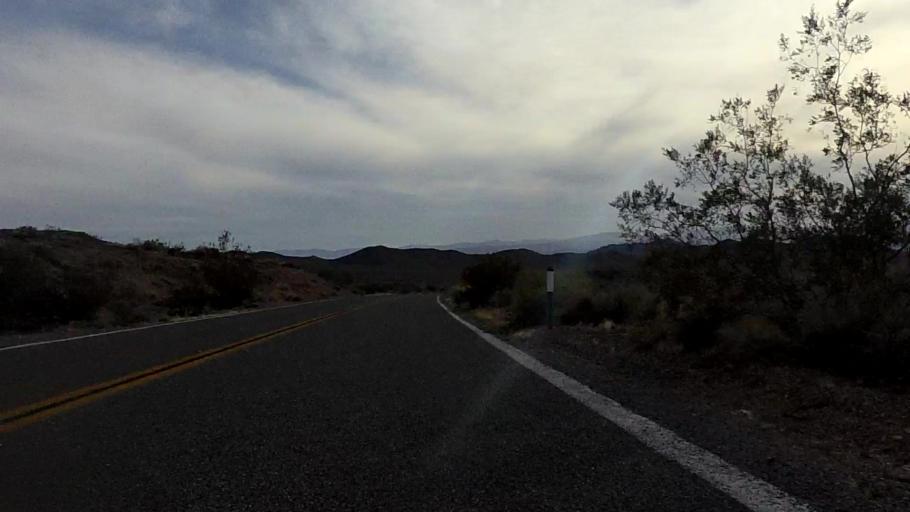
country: US
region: Nevada
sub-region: Nye County
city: Pahrump
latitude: 35.9187
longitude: -116.4367
